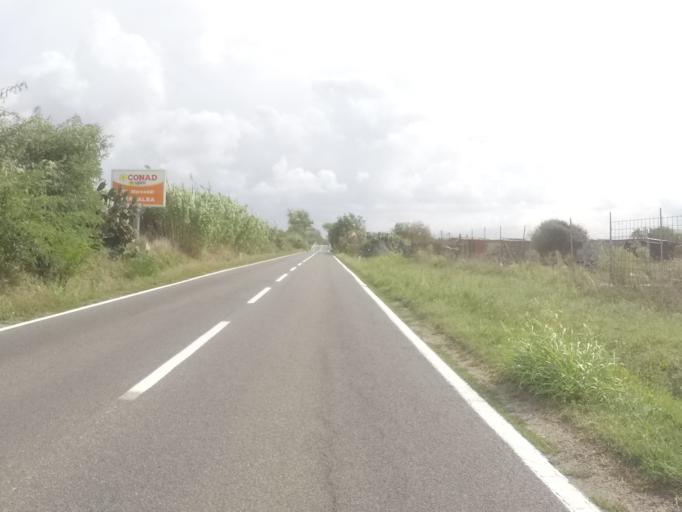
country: IT
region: Sardinia
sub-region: Provincia di Oristano
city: Terralba
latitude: 39.7035
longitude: 8.6395
